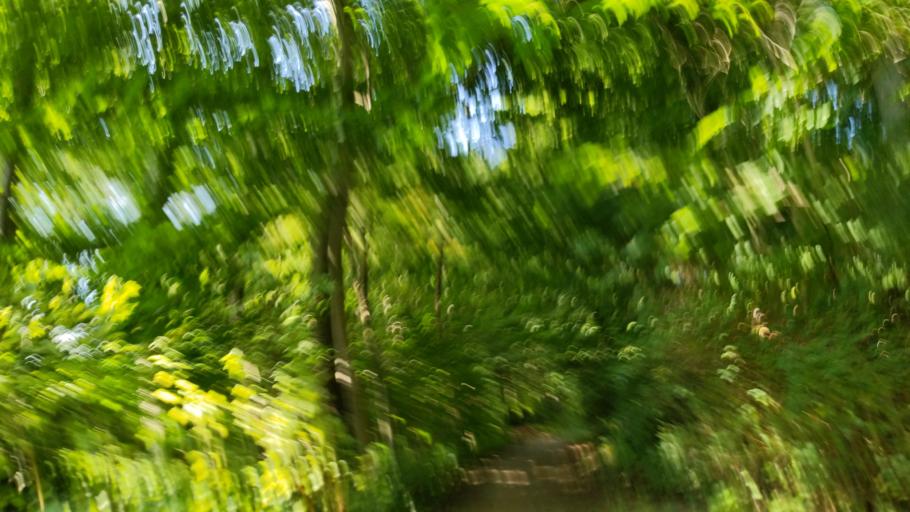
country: DE
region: Schleswig-Holstein
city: Malente
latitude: 54.1844
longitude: 10.5949
